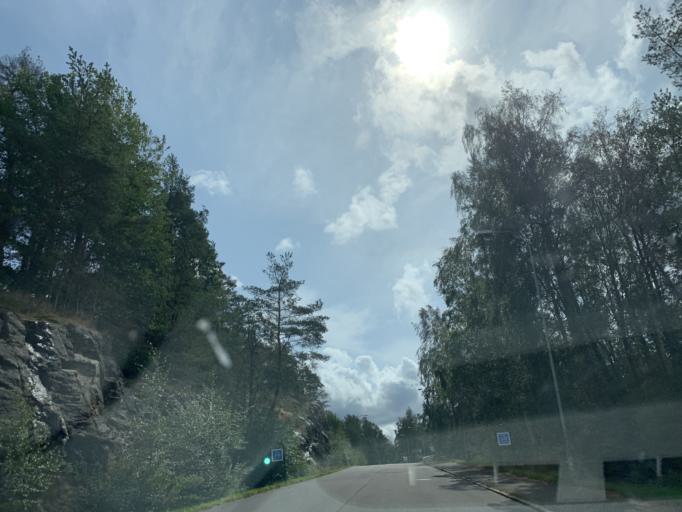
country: SE
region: Vaestra Goetaland
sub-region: Goteborg
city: Eriksbo
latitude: 57.7620
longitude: 12.0571
